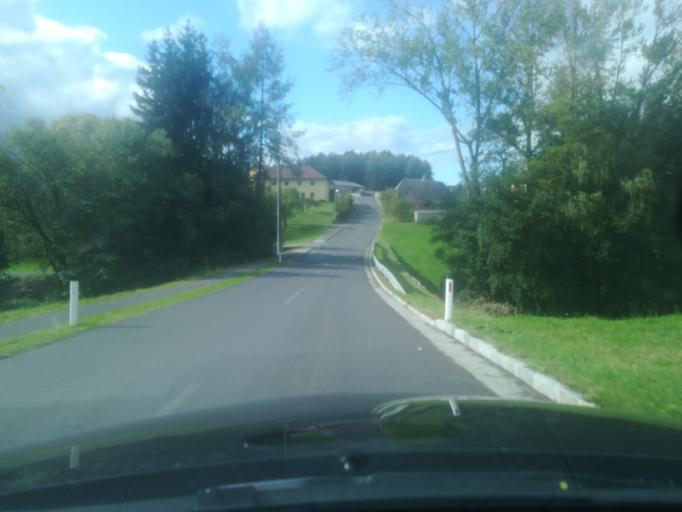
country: AT
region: Upper Austria
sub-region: Politischer Bezirk Urfahr-Umgebung
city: Herzogsdorf
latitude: 48.4297
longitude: 14.1242
